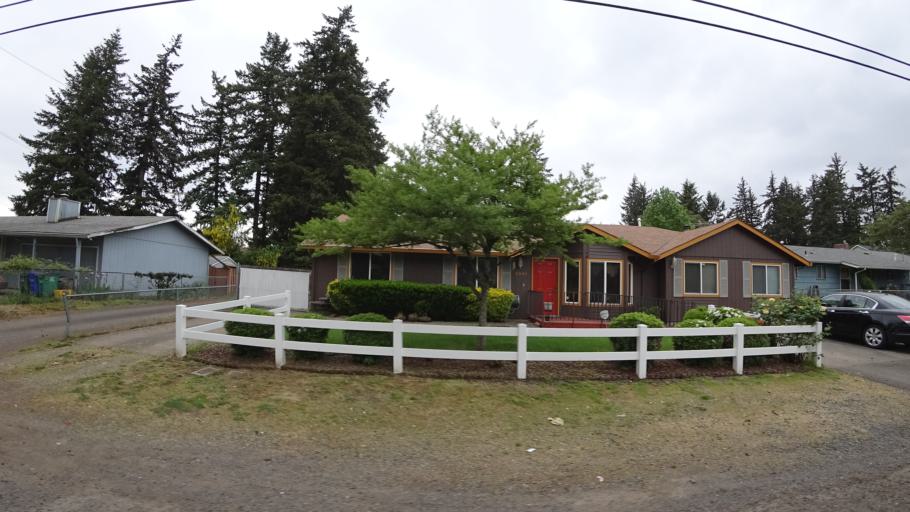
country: US
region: Oregon
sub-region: Multnomah County
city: Lents
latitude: 45.5054
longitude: -122.5156
